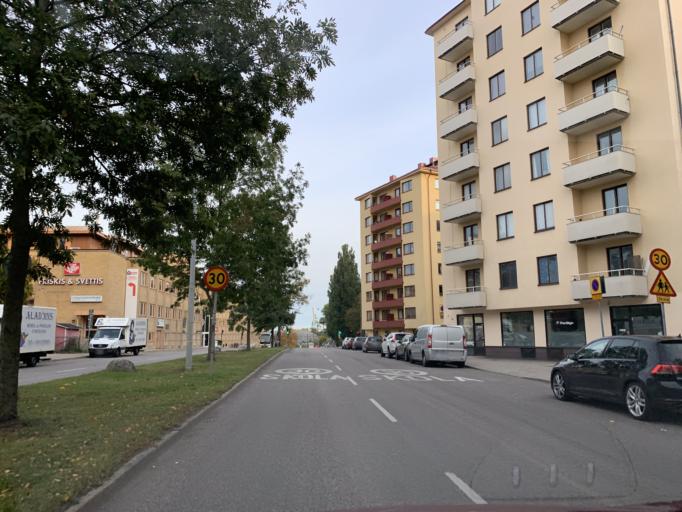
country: SE
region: Stockholm
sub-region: Stockholms Kommun
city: OEstermalm
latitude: 59.3479
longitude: 18.1061
